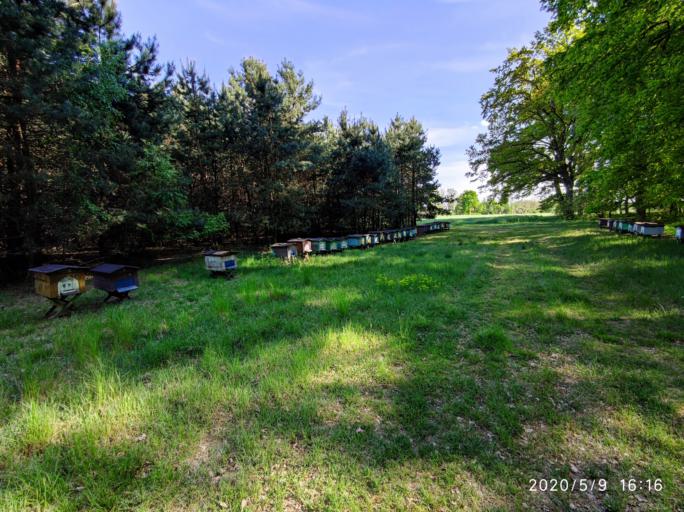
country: PL
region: Lubusz
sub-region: Powiat zielonogorski
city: Babimost
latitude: 52.1723
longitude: 15.8148
